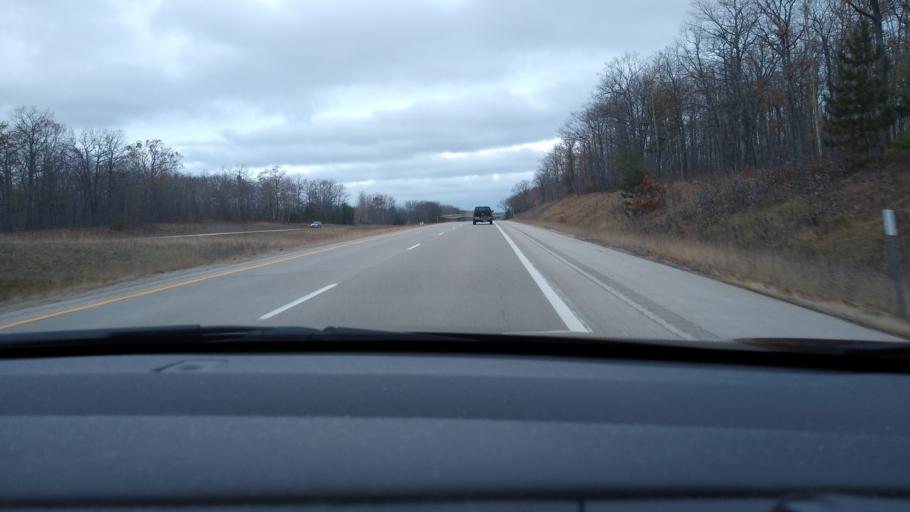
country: US
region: Michigan
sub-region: Cheboygan County
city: Indian River
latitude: 45.4920
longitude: -84.6152
